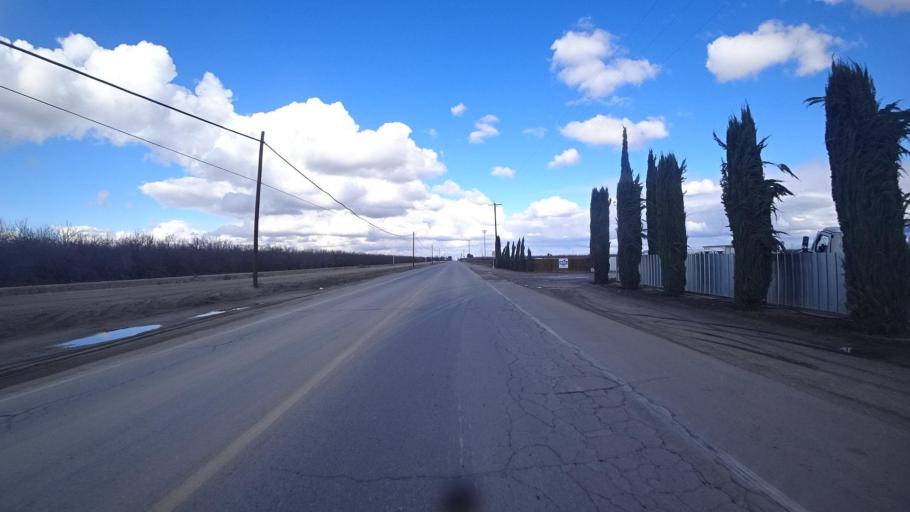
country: US
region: California
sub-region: Kern County
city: Greenfield
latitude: 35.2095
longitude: -119.1099
